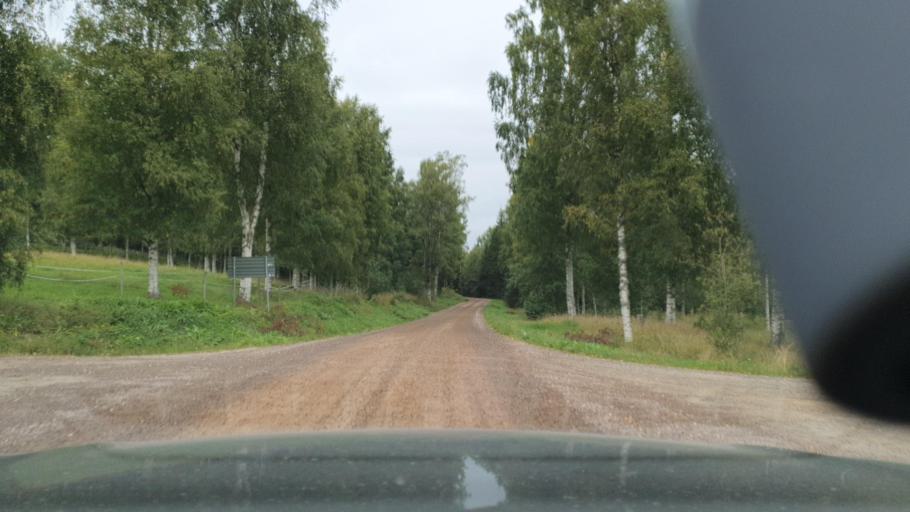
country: SE
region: Vaermland
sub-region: Arvika Kommun
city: Arvika
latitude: 59.9992
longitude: 12.6588
